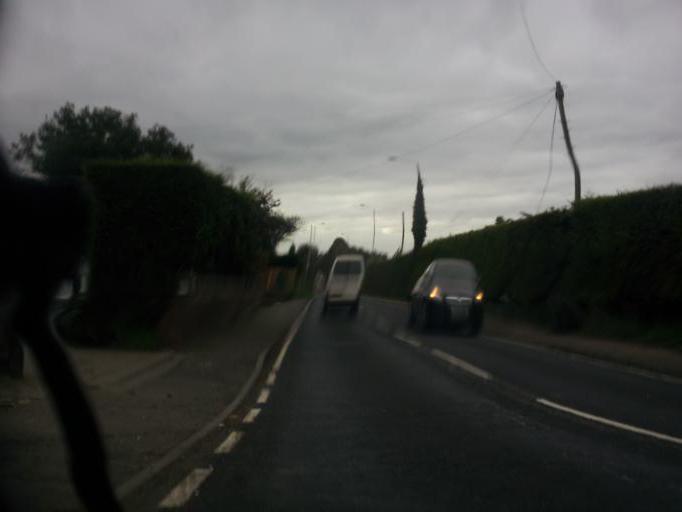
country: GB
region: England
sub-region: Kent
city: Newington
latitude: 51.3540
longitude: 0.6571
